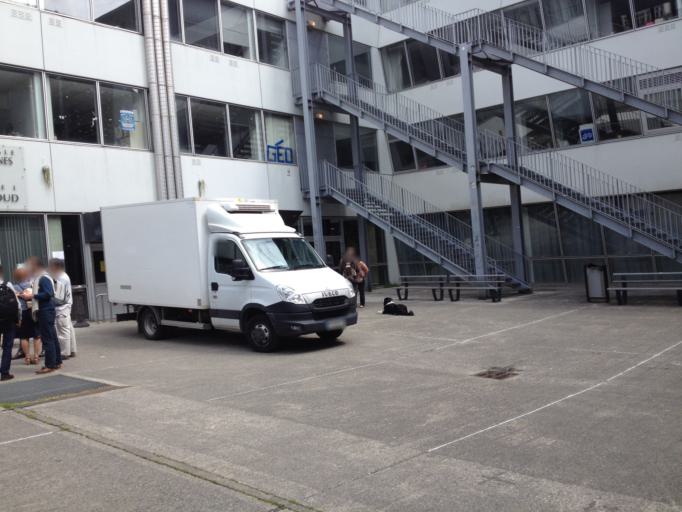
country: FR
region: Brittany
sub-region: Departement du Finistere
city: Brest
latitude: 48.3919
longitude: -4.4886
